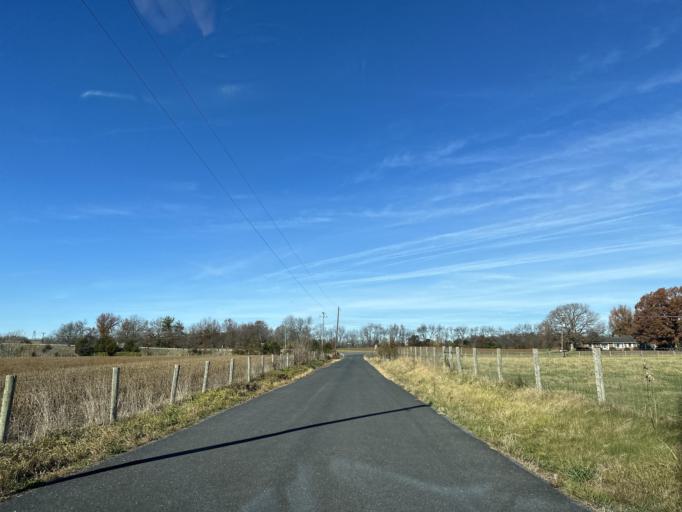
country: US
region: Virginia
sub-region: Augusta County
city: Weyers Cave
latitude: 38.2703
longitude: -78.9330
